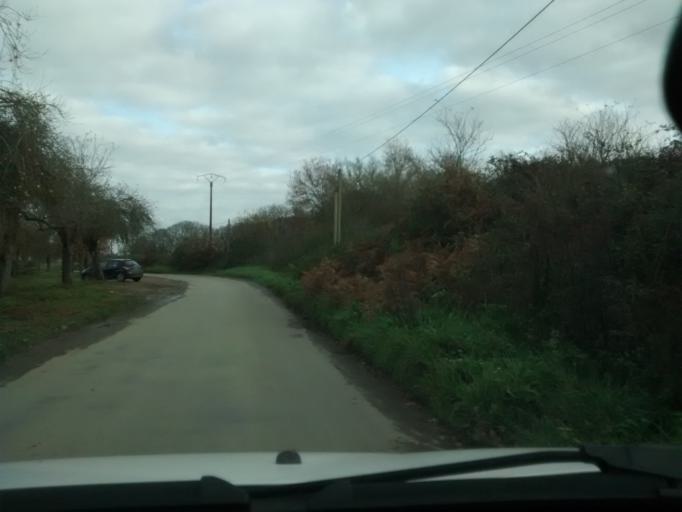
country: FR
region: Brittany
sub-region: Departement d'Ille-et-Vilaine
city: Saint-Jacques-de-la-Lande
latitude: 48.0881
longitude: -1.7426
